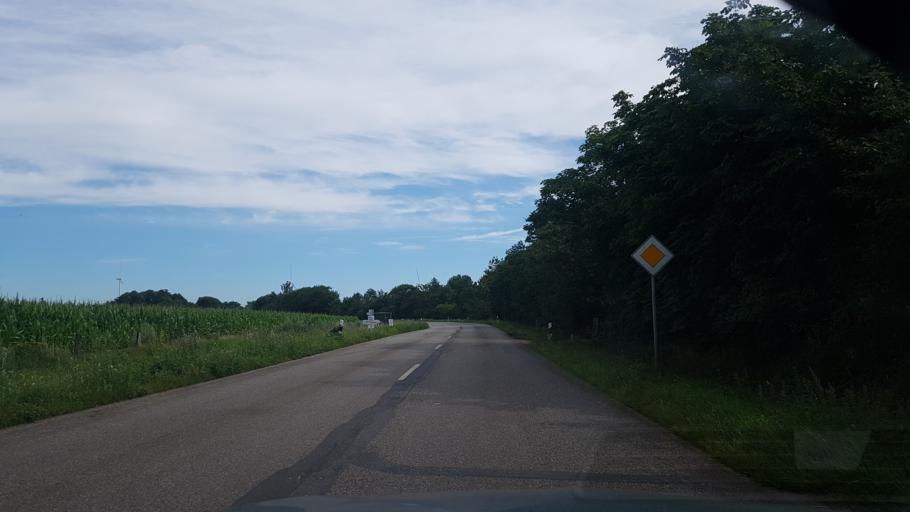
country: DE
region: Schleswig-Holstein
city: Bramstedtlund
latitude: 54.8602
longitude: 9.0449
